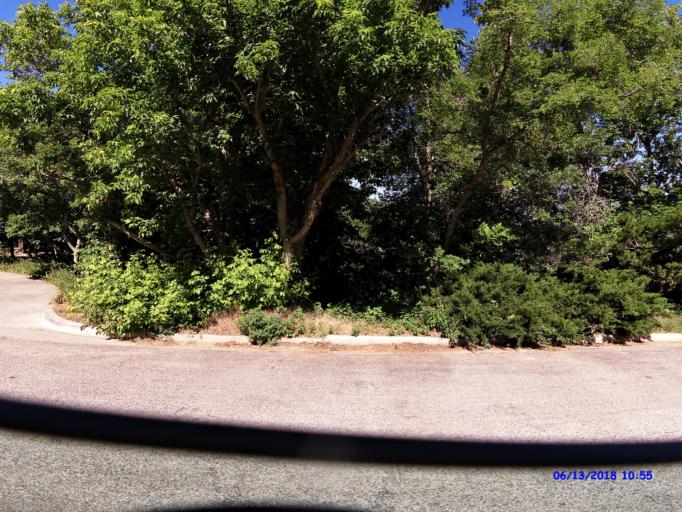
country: US
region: Utah
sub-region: Weber County
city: South Ogden
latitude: 41.2003
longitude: -111.9393
